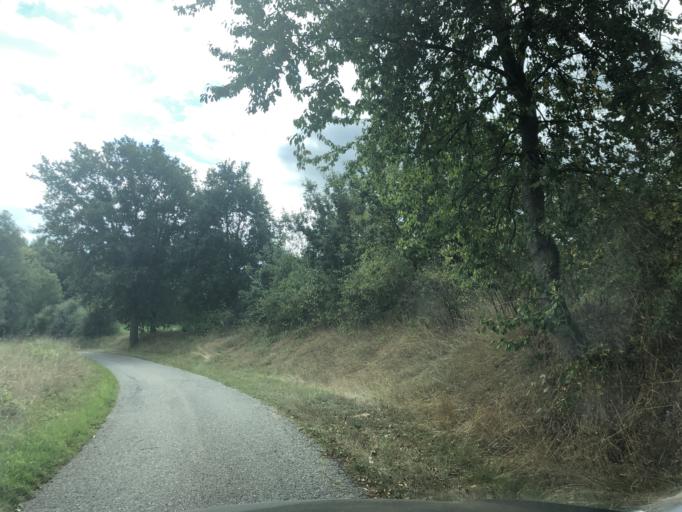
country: DE
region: Bavaria
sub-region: Upper Palatinate
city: Pressath
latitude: 49.7597
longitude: 11.9291
